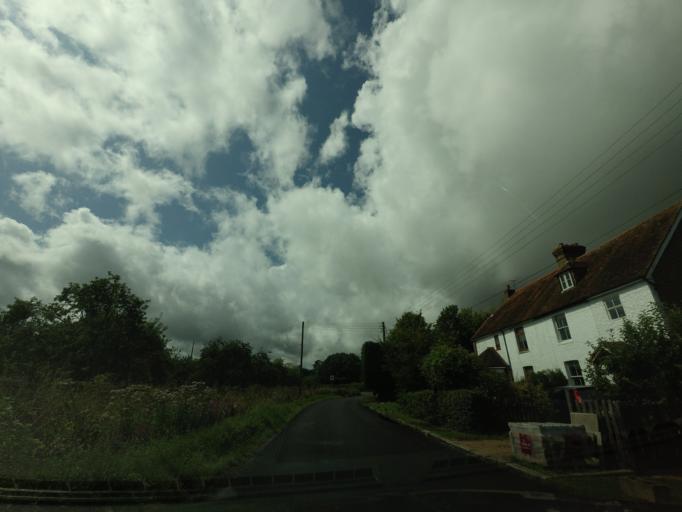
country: GB
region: England
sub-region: Kent
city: Paddock Wood
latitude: 51.1840
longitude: 0.4086
